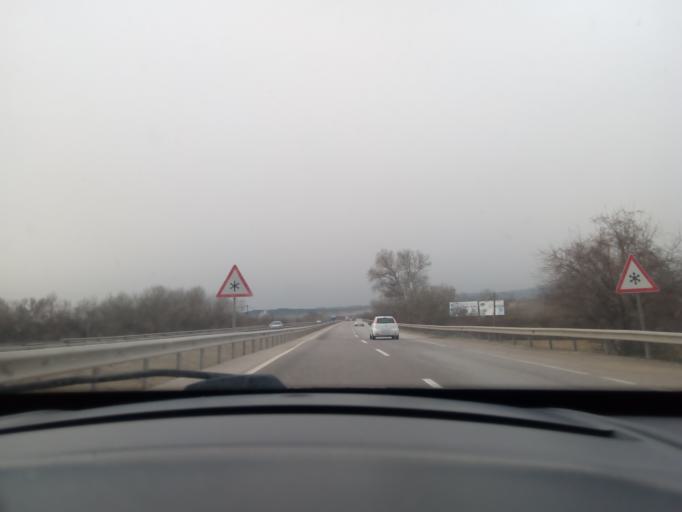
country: TR
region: Balikesir
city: Gobel
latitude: 39.9815
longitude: 28.1882
